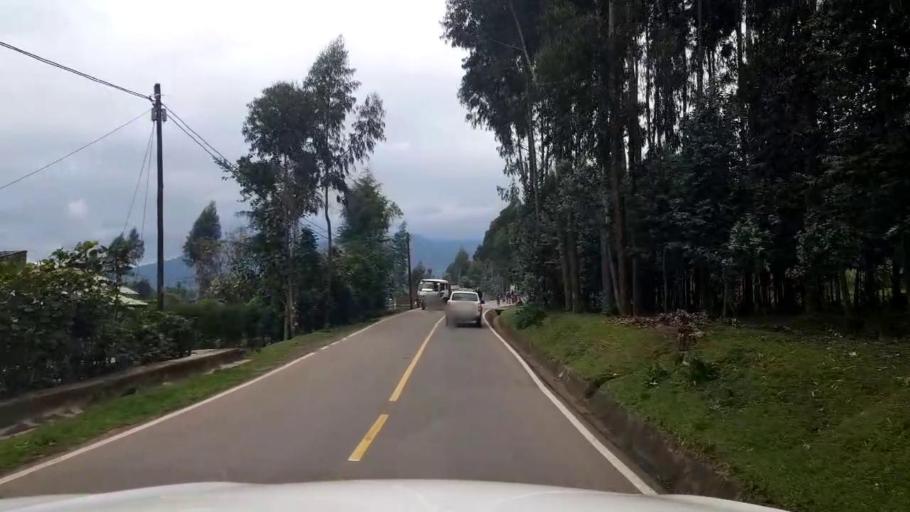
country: RW
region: Northern Province
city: Musanze
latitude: -1.4359
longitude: 29.5546
